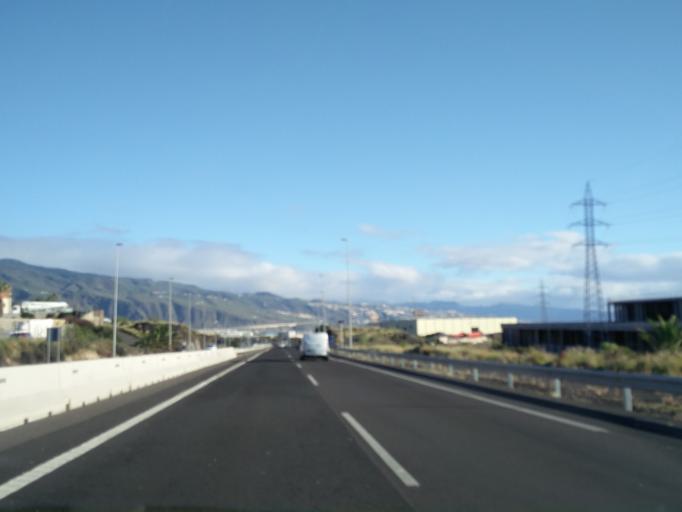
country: ES
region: Canary Islands
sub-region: Provincia de Santa Cruz de Tenerife
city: Candelaria
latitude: 28.3258
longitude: -16.3769
